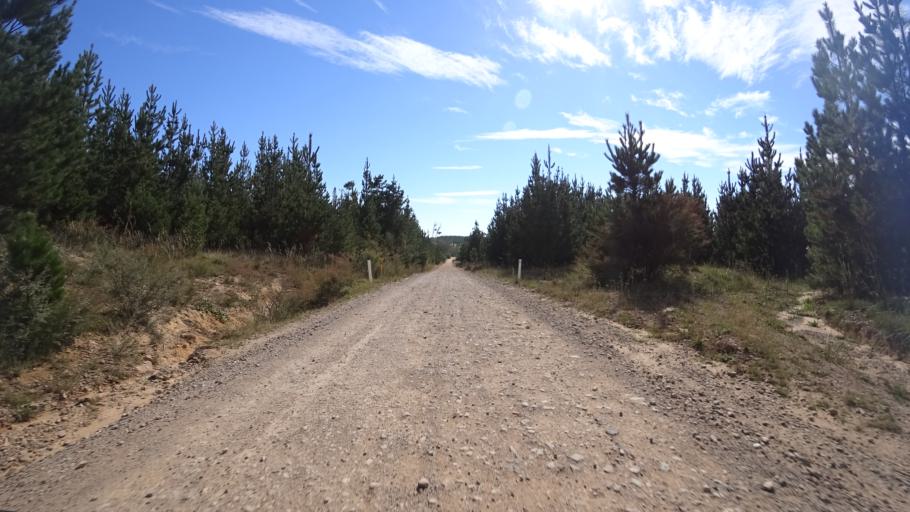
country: AU
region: New South Wales
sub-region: Lithgow
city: Lithgow
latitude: -33.3600
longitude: 150.2498
